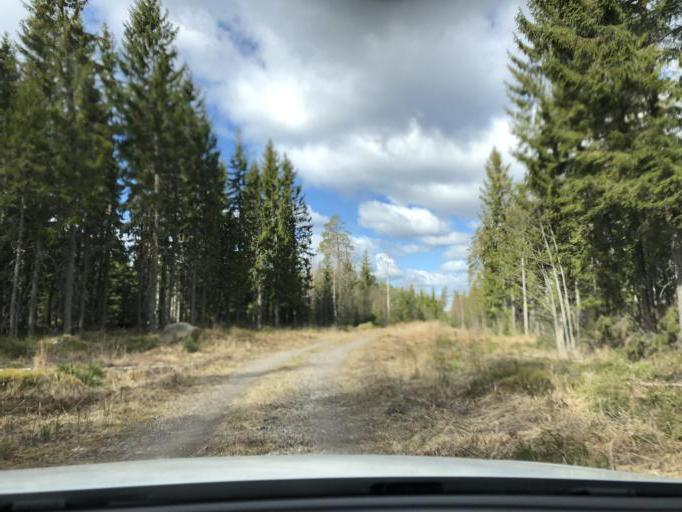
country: SE
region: Uppsala
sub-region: Tierps Kommun
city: Tierp
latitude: 60.3294
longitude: 17.3415
